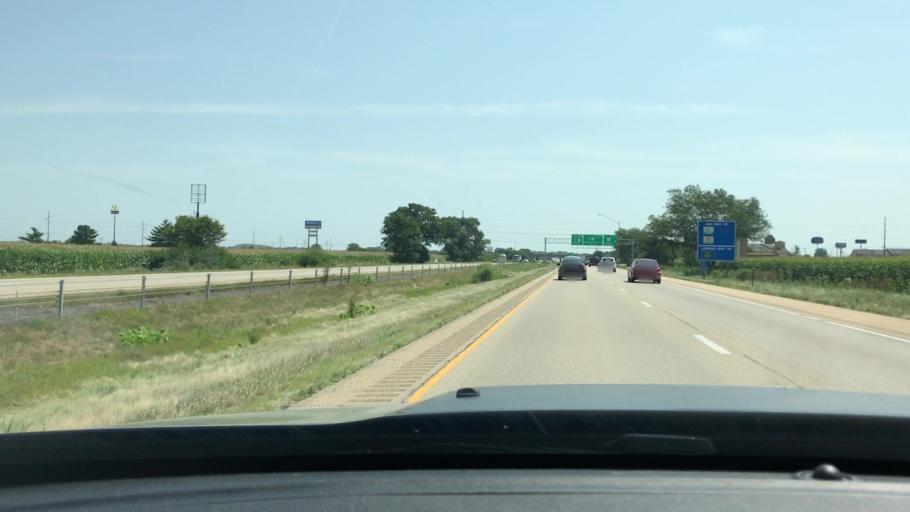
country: US
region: Illinois
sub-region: LaSalle County
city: Peru
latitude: 41.3651
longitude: -89.1342
